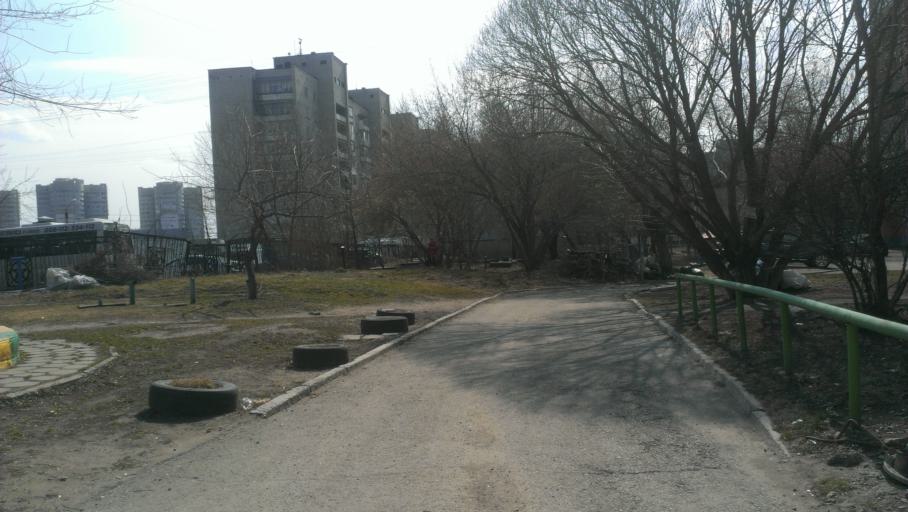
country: RU
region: Altai Krai
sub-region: Gorod Barnaulskiy
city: Barnaul
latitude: 53.3455
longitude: 83.6942
